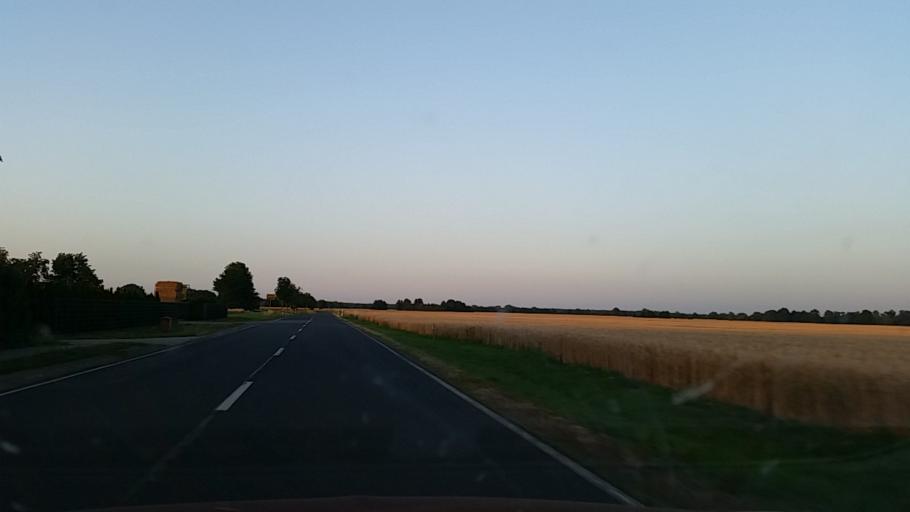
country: DE
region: Saxony-Anhalt
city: Prettin
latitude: 51.7240
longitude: 12.9418
